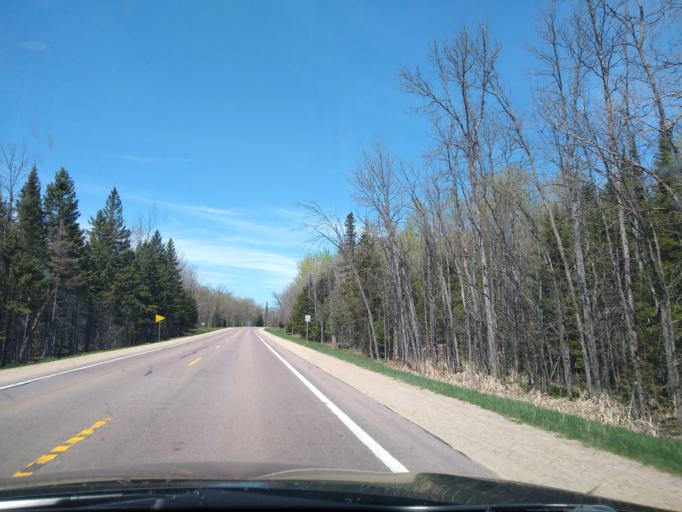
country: US
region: Michigan
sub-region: Marquette County
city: K. I. Sawyer Air Force Base
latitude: 46.2300
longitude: -87.0661
